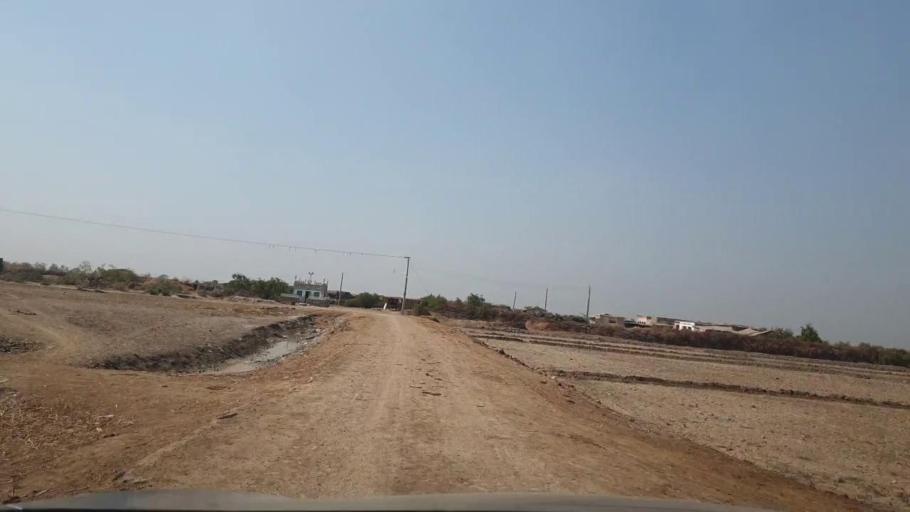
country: PK
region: Sindh
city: Berani
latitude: 25.6629
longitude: 68.8686
